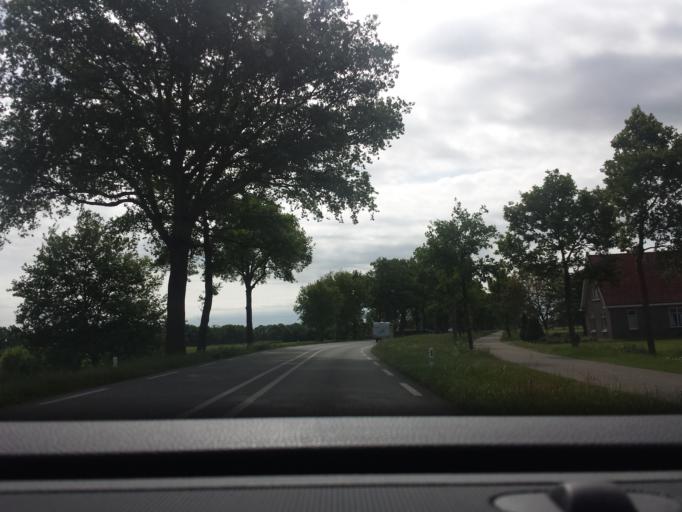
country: NL
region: Gelderland
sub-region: Gemeente Lochem
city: Barchem
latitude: 52.0758
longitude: 6.4705
